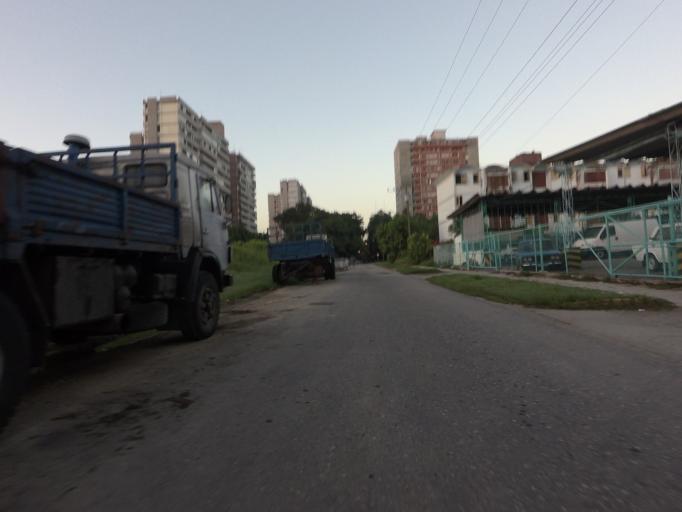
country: CU
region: La Habana
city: Havana
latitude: 23.1210
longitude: -82.3920
